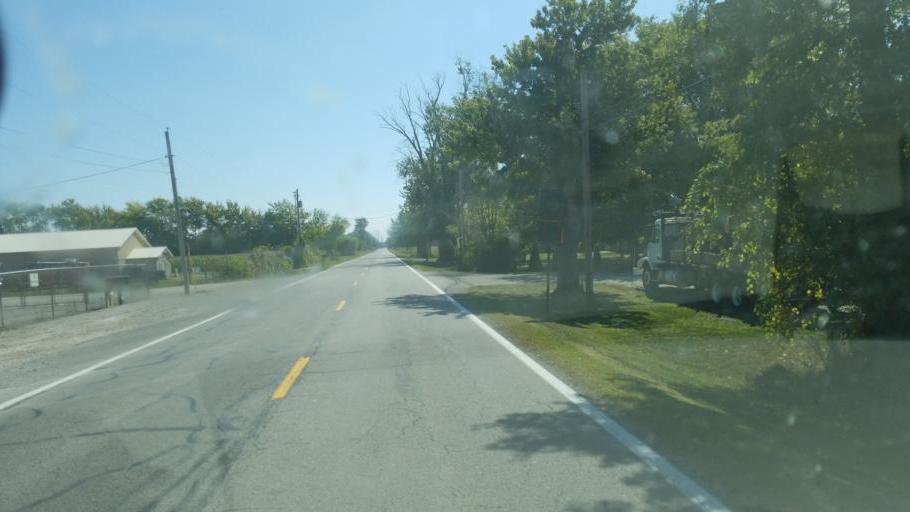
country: US
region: Ohio
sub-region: Marion County
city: Marion
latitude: 40.5996
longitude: -83.1619
